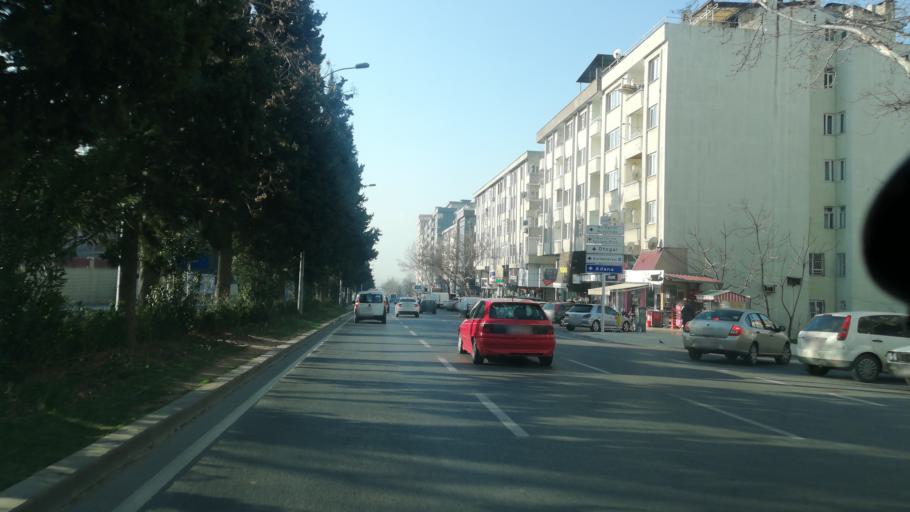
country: TR
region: Kahramanmaras
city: Kahramanmaras
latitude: 37.5737
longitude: 36.9259
